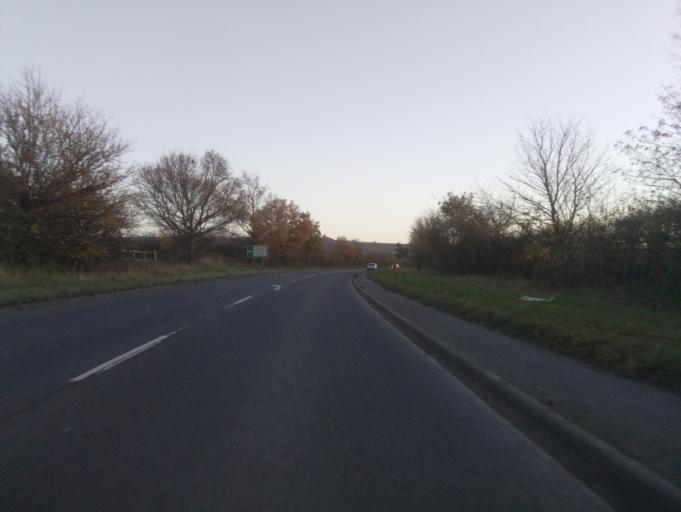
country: GB
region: England
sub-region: Wiltshire
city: Westbury
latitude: 51.2776
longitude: -2.1804
